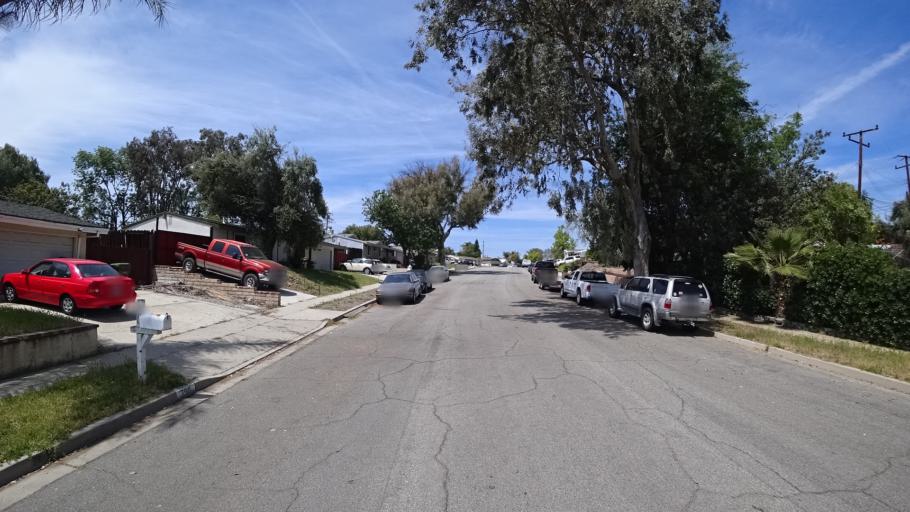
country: US
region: California
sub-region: Ventura County
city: Thousand Oaks
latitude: 34.1912
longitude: -118.8637
